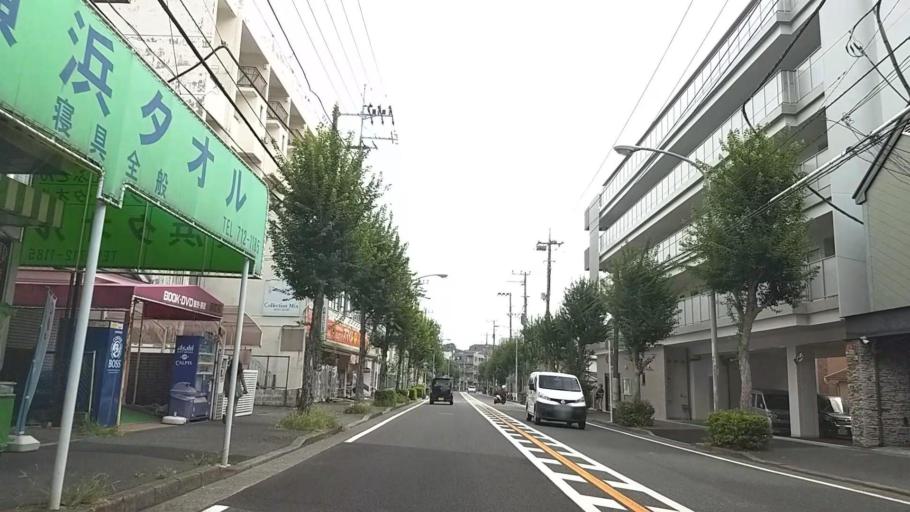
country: JP
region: Kanagawa
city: Yokohama
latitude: 35.4240
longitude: 139.5895
